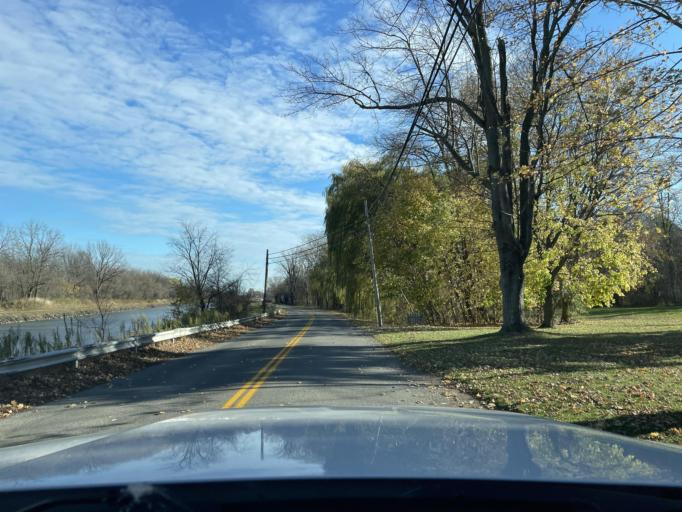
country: US
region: New York
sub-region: Niagara County
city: Gasport
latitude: 43.2025
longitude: -78.5543
